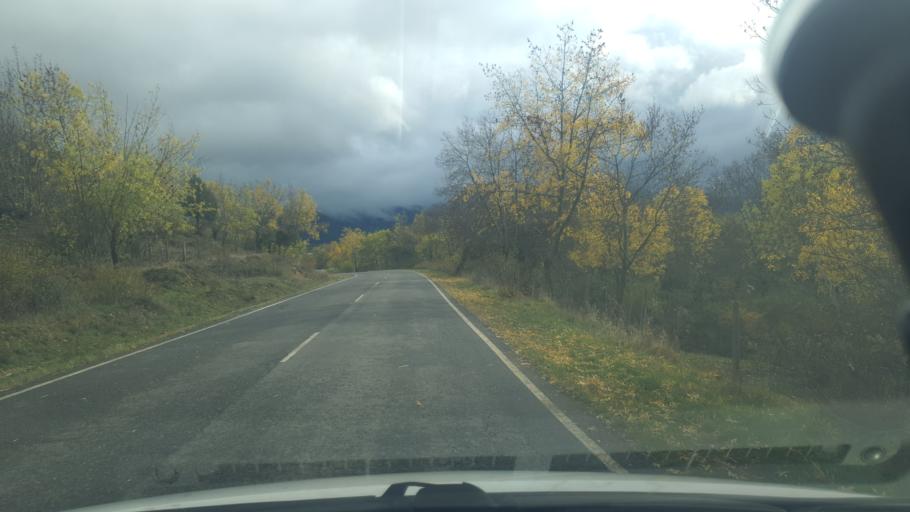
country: ES
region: Castille and Leon
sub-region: Provincia de Segovia
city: Gallegos
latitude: 41.0817
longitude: -3.7914
